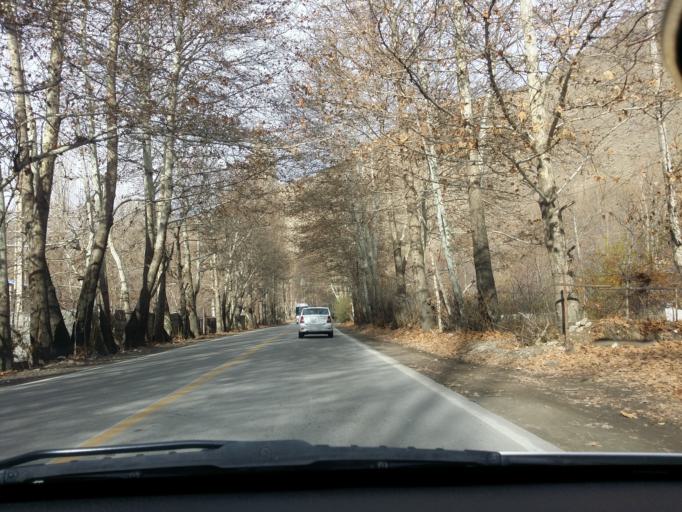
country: IR
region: Tehran
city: Tajrish
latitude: 36.0272
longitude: 51.2440
